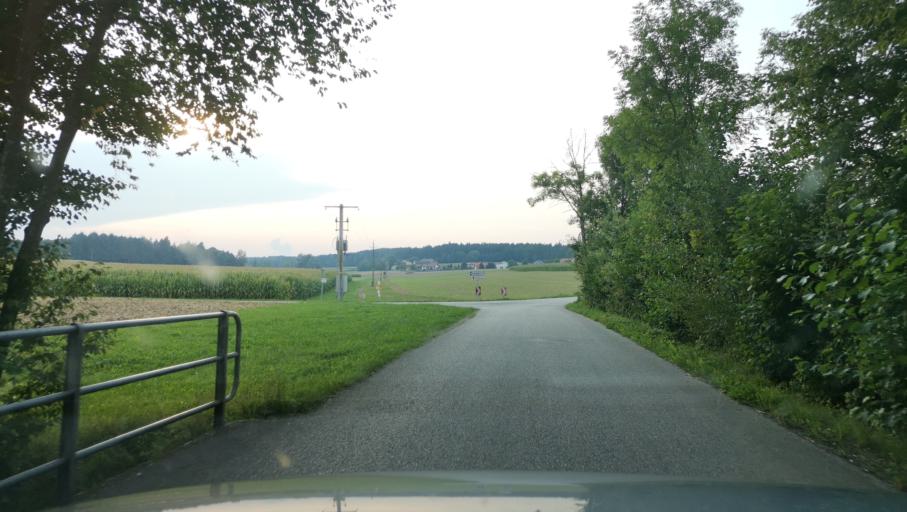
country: AT
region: Upper Austria
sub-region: Politischer Bezirk Grieskirchen
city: Grieskirchen
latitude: 48.2980
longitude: 13.8189
